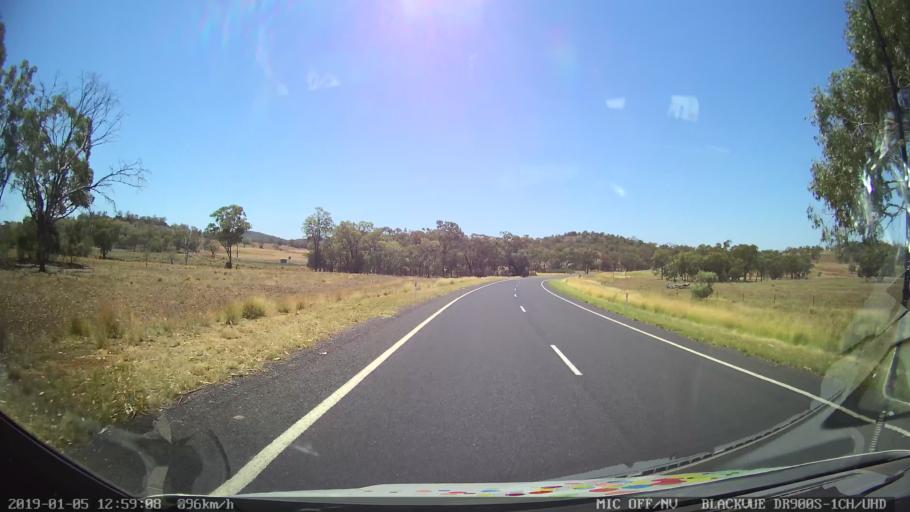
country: AU
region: New South Wales
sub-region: Narrabri
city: Boggabri
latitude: -31.1120
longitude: 149.7609
